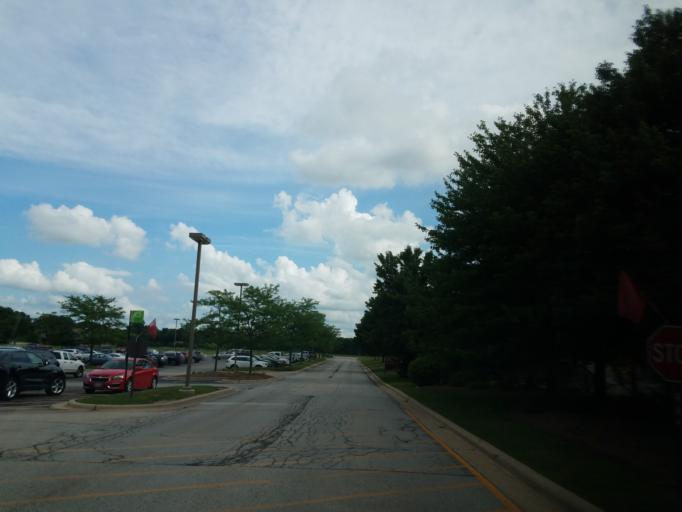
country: US
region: Illinois
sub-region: McLean County
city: Normal
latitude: 40.5094
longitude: -88.9494
